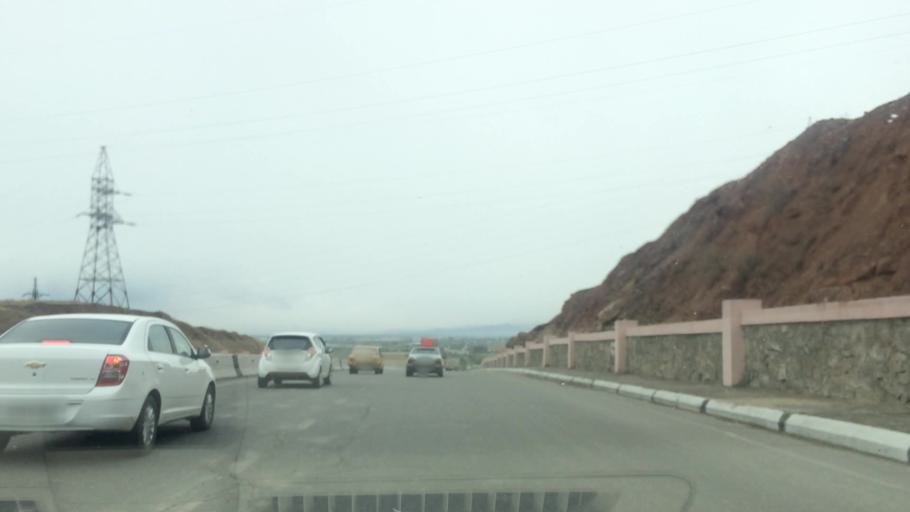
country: UZ
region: Samarqand
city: Jomboy
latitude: 39.6858
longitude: 67.0519
